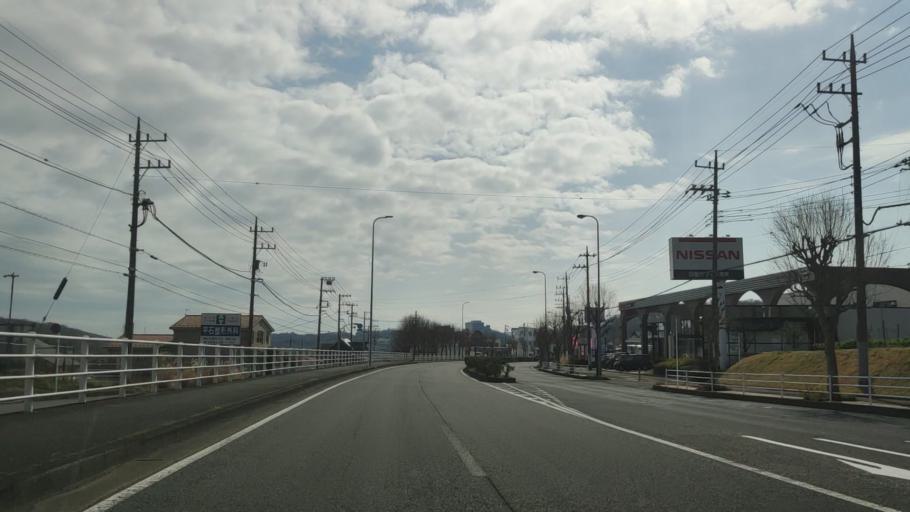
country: JP
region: Kanagawa
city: Hadano
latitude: 35.3502
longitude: 139.2354
